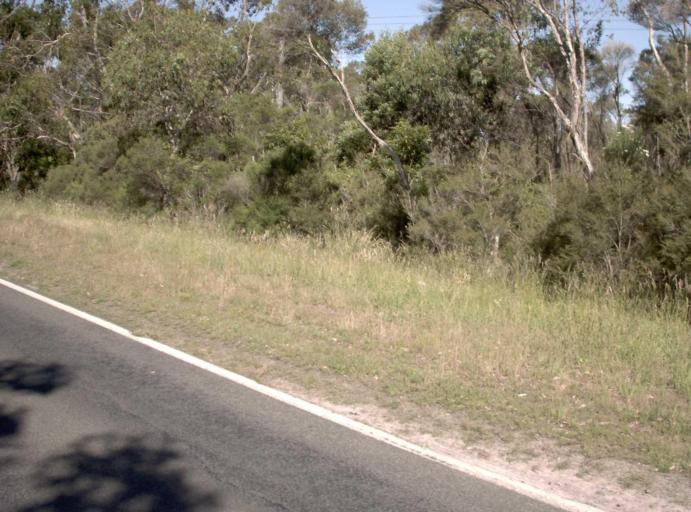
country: AU
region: Victoria
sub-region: Latrobe
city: Morwell
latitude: -38.6441
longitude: 146.5121
